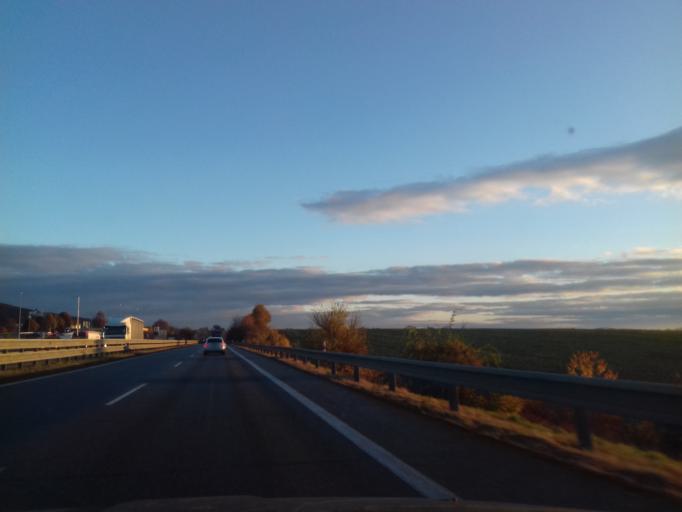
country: CZ
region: South Moravian
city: Pustimer
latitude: 49.3164
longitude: 17.0370
